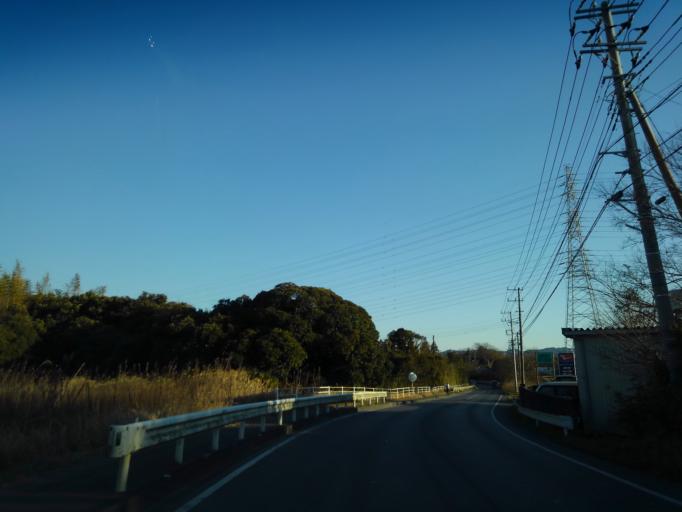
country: JP
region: Chiba
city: Kimitsu
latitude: 35.3122
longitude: 139.9363
